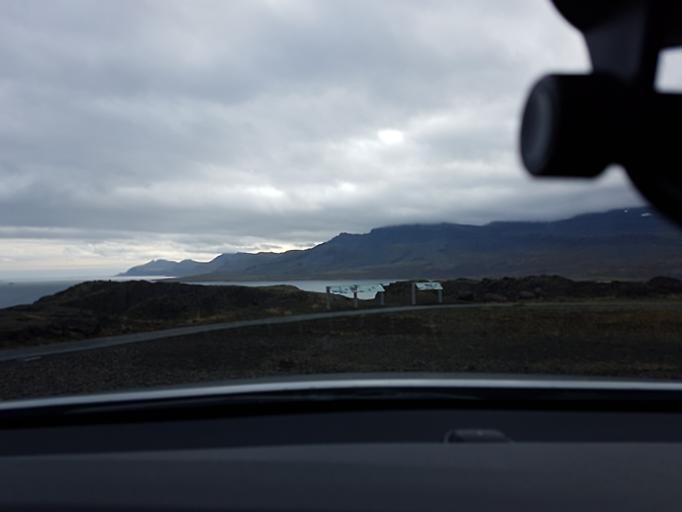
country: IS
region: East
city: Eskifjoerdur
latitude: 65.0460
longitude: -14.0155
